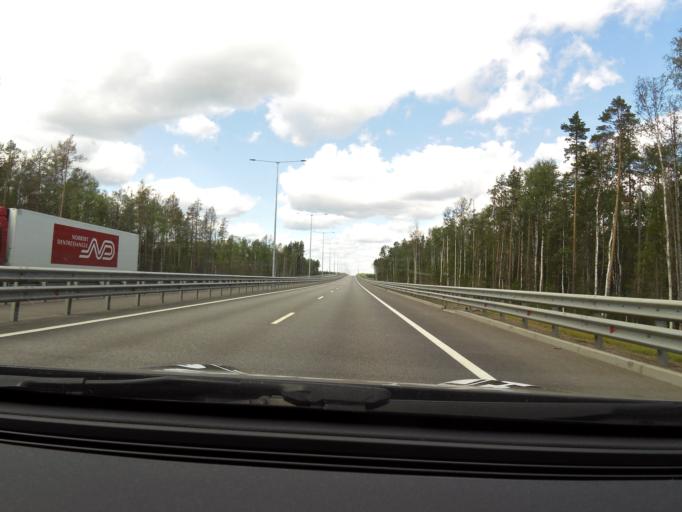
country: RU
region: Tverskaya
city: Vyshniy Volochek
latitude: 57.4309
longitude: 34.4711
